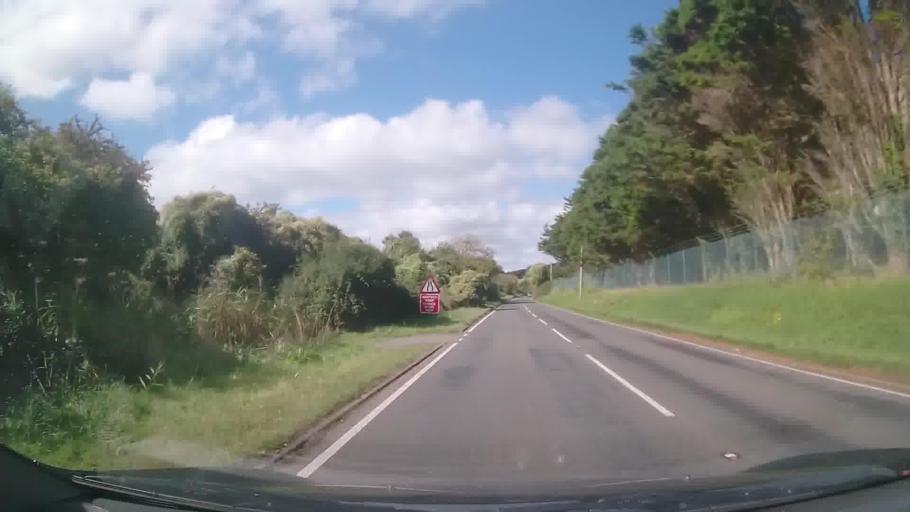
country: GB
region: Wales
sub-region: Pembrokeshire
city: Penally
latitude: 51.6562
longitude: -4.7350
